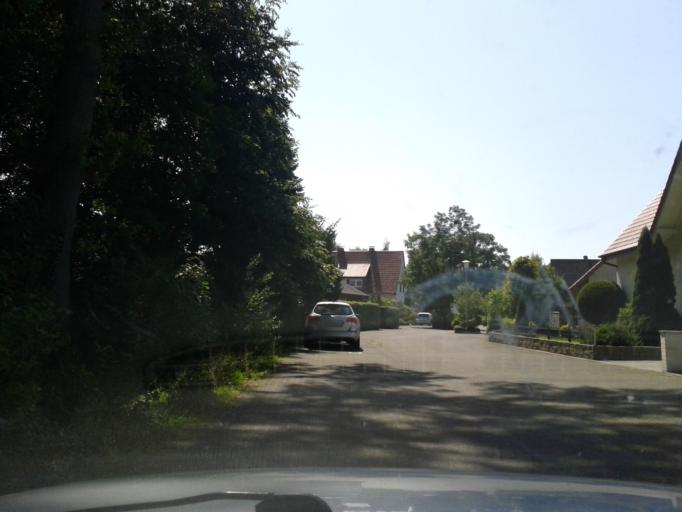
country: DE
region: North Rhine-Westphalia
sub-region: Regierungsbezirk Detmold
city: Paderborn
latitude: 51.7504
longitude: 8.7375
